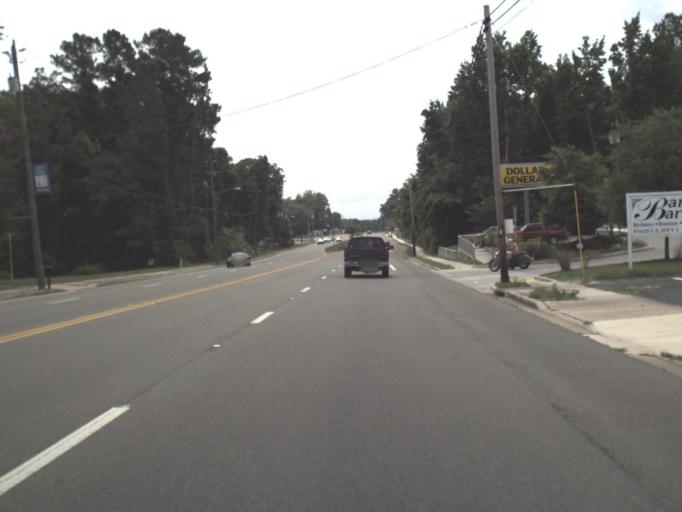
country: US
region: Florida
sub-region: Nassau County
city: Hilliard
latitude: 30.6880
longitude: -81.9158
